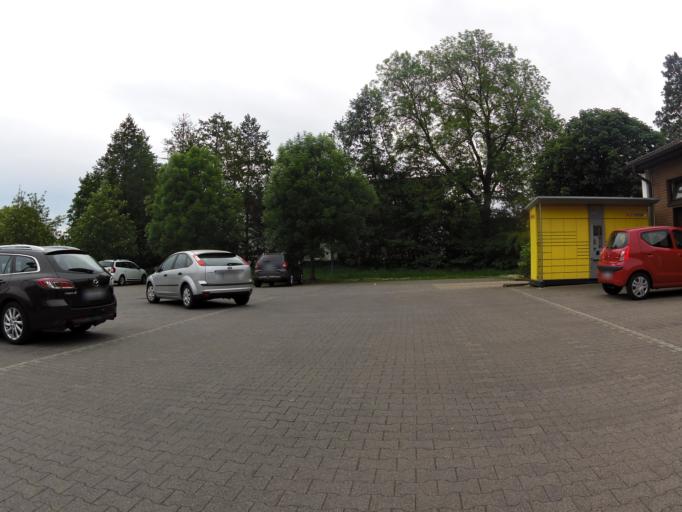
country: DE
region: North Rhine-Westphalia
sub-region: Regierungsbezirk Detmold
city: Hoexter
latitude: 51.7840
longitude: 9.3813
